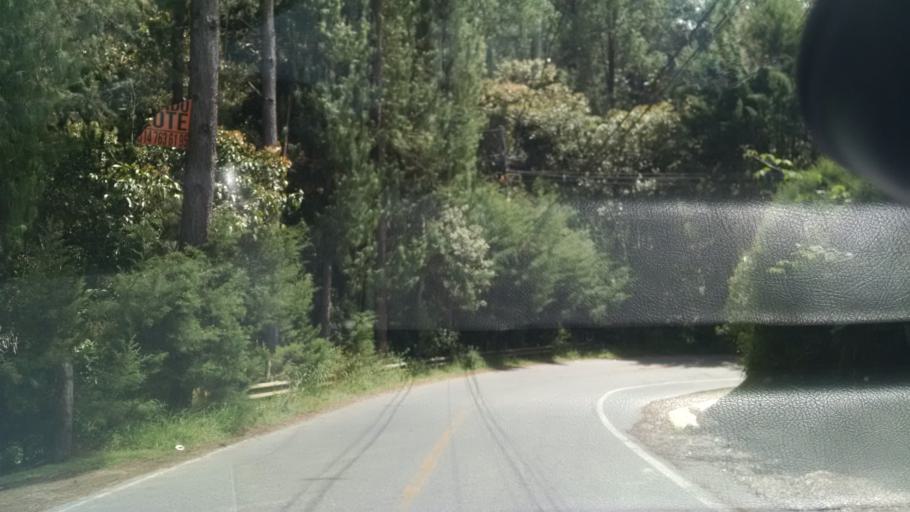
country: CO
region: Antioquia
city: El Retiro
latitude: 6.0839
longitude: -75.5015
